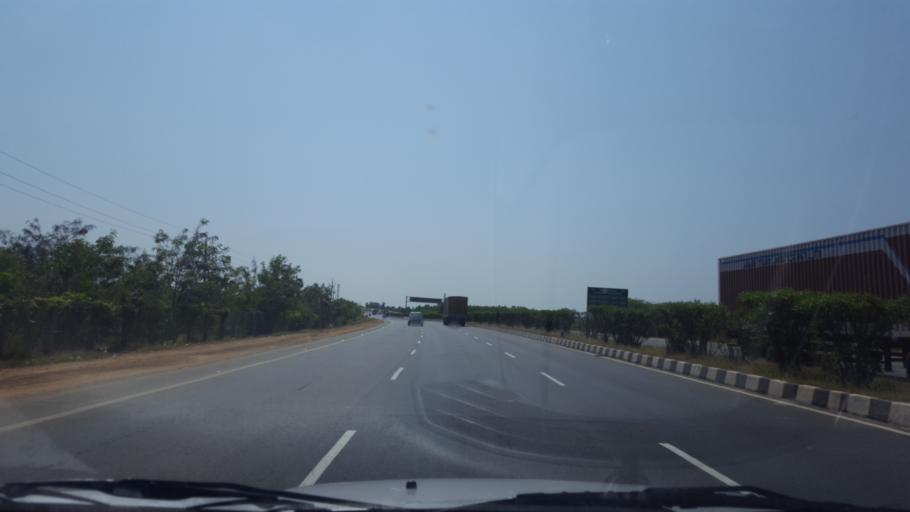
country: IN
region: Andhra Pradesh
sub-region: Prakasam
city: Singarayakonda
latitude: 15.3257
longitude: 80.0280
